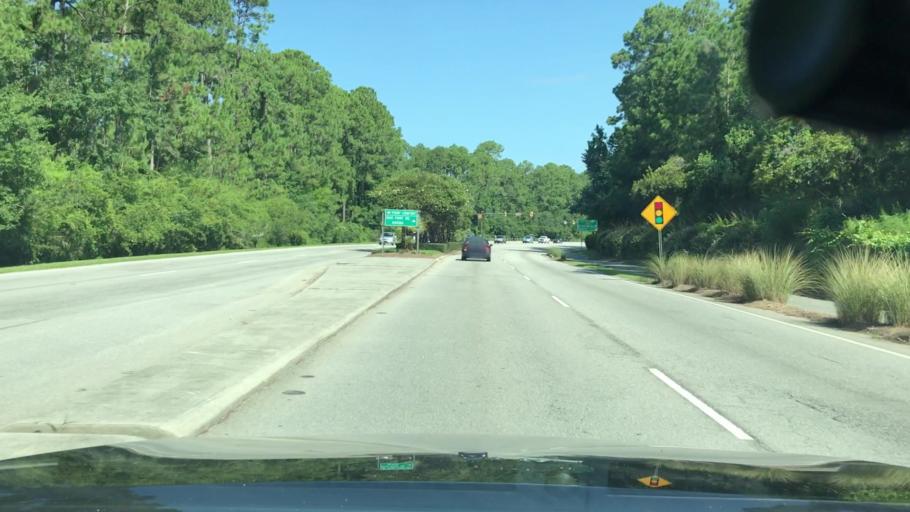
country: US
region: South Carolina
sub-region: Beaufort County
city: Hilton Head Island
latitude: 32.1671
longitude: -80.7723
